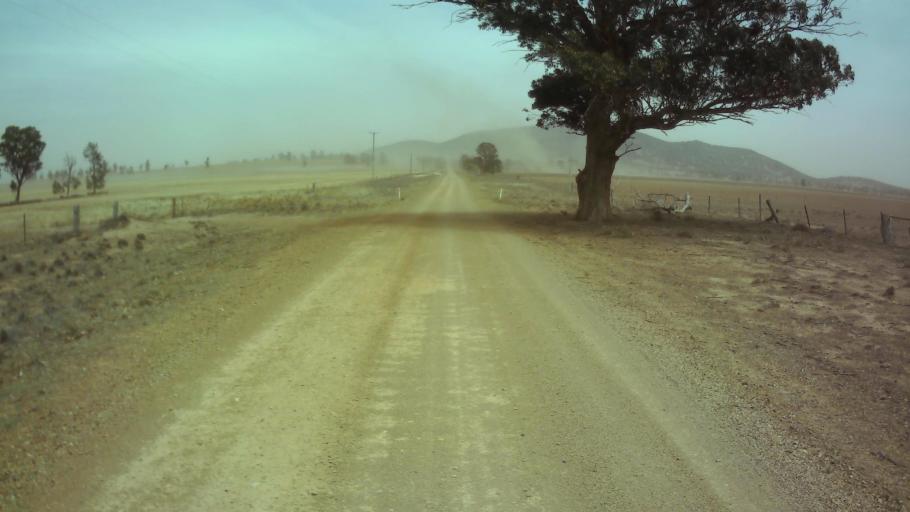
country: AU
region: New South Wales
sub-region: Weddin
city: Grenfell
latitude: -33.7462
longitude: 147.9844
